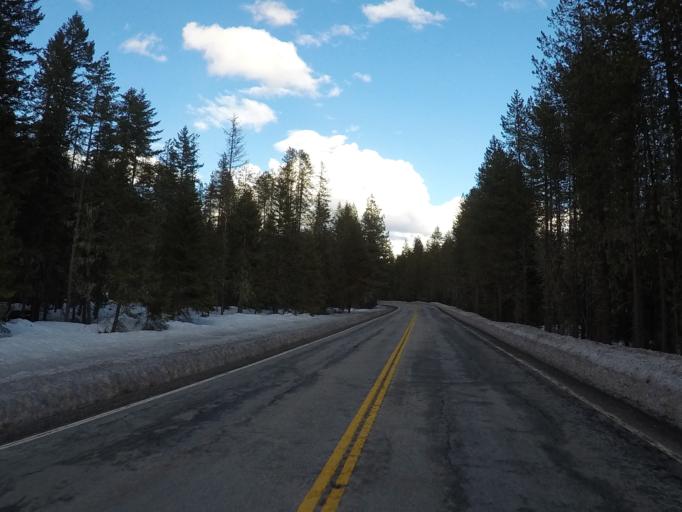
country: US
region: Montana
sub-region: Ravalli County
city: Hamilton
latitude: 46.5090
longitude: -114.7675
